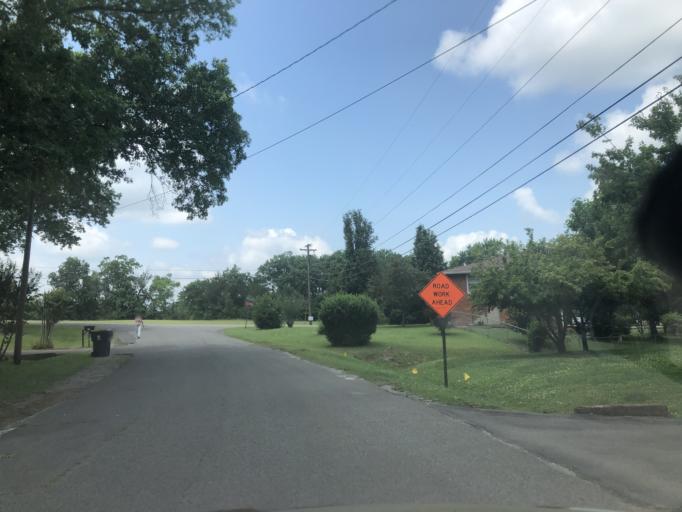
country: US
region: Tennessee
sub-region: Davidson County
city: Lakewood
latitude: 36.2070
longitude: -86.6371
